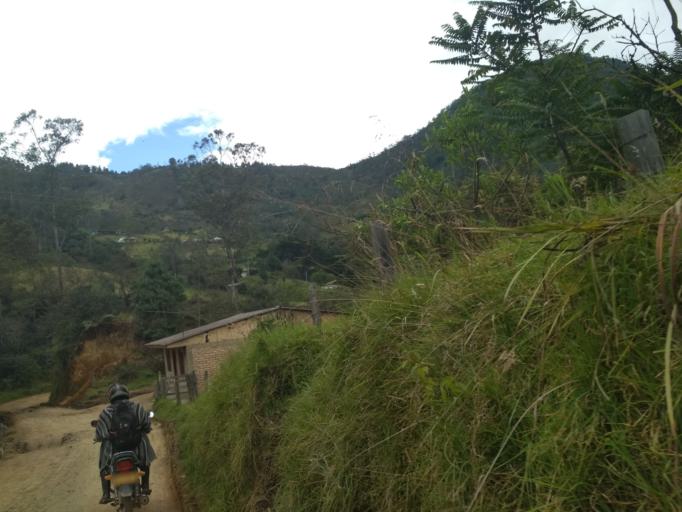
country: CO
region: Cauca
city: Jambalo
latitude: 2.7154
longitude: -76.3246
